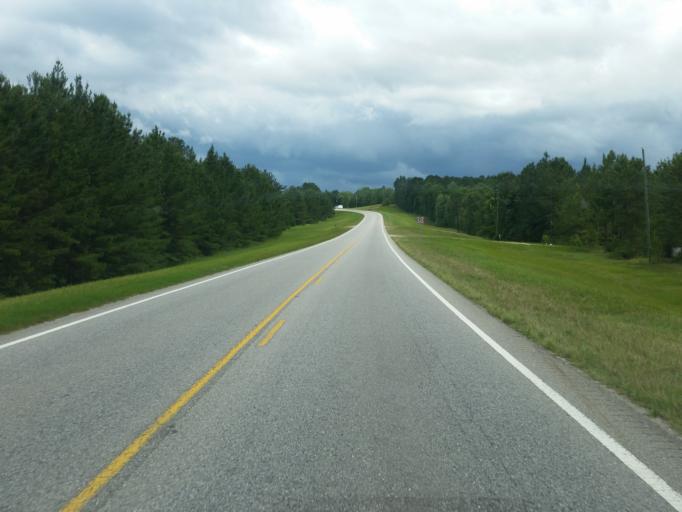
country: US
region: Mississippi
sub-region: George County
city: Lucedale
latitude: 30.8563
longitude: -88.4088
